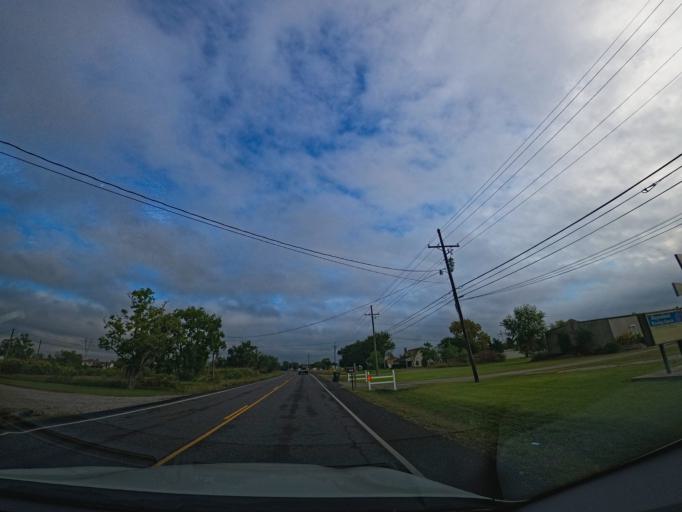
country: US
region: Louisiana
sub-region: Terrebonne Parish
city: Dulac
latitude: 29.4468
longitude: -90.7024
